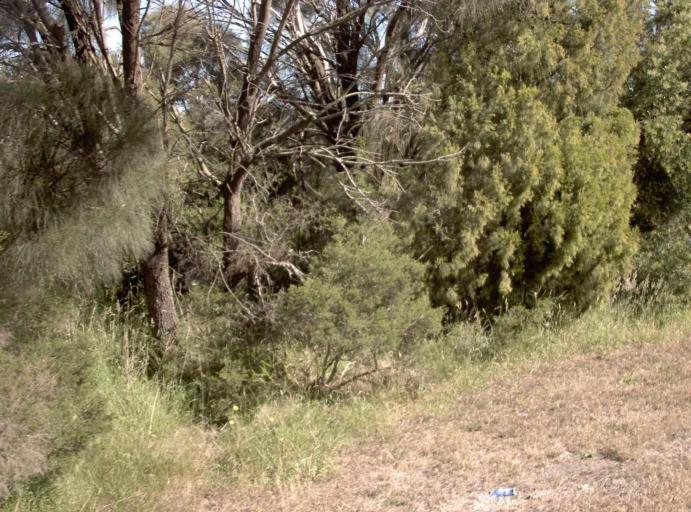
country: AU
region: Victoria
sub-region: Latrobe
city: Traralgon
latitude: -38.6373
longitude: 146.6735
